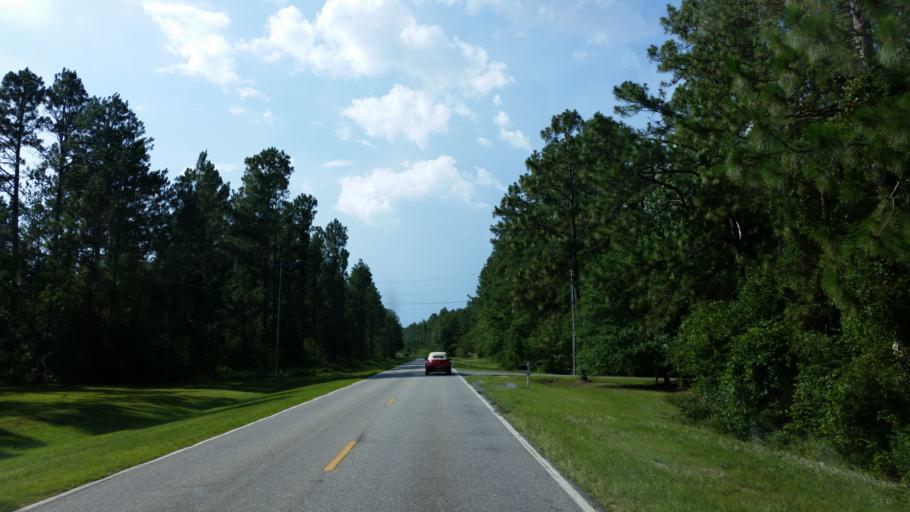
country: US
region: Georgia
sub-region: Lowndes County
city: Hahira
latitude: 30.9064
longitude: -83.3819
